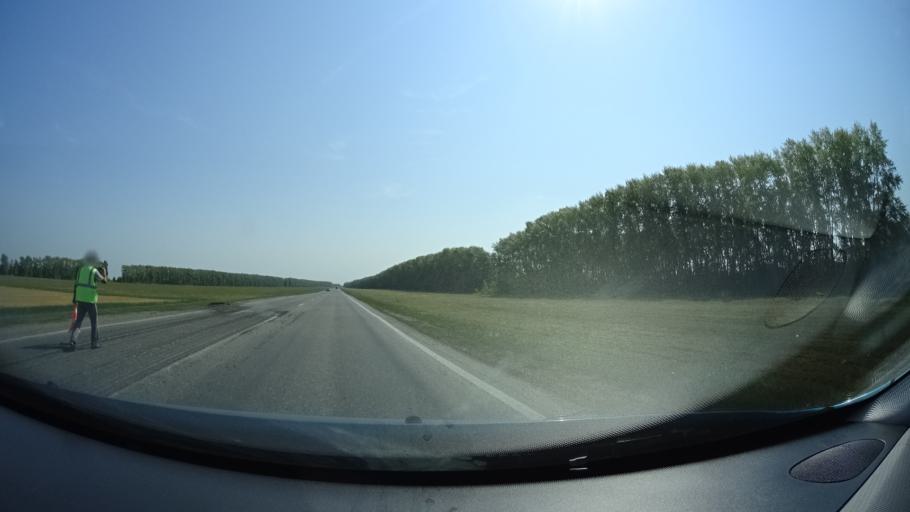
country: RU
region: Bashkortostan
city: Karmaskaly
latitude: 54.3988
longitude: 56.0985
